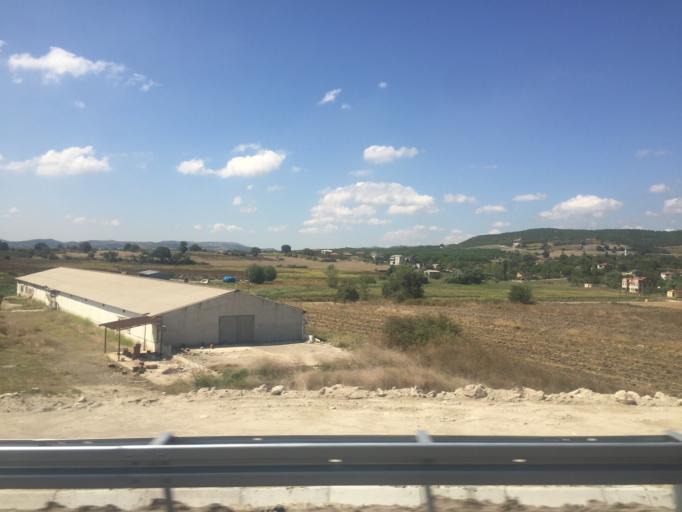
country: TR
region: Balikesir
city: Susurluk
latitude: 39.9586
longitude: 28.1668
